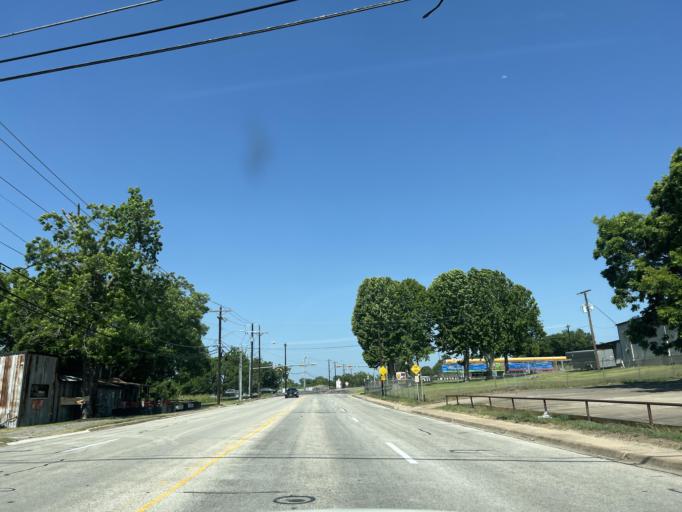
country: US
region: Texas
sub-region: Washington County
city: Brenham
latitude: 30.1698
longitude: -96.3828
